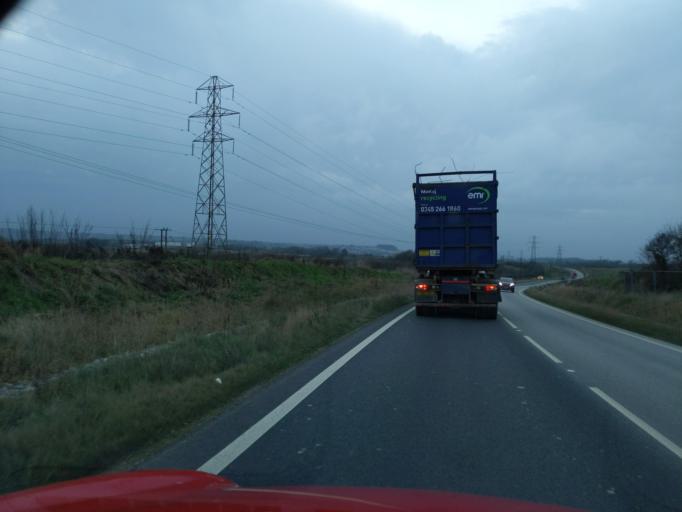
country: GB
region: England
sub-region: Devon
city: Plympton
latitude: 50.3728
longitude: -4.0341
